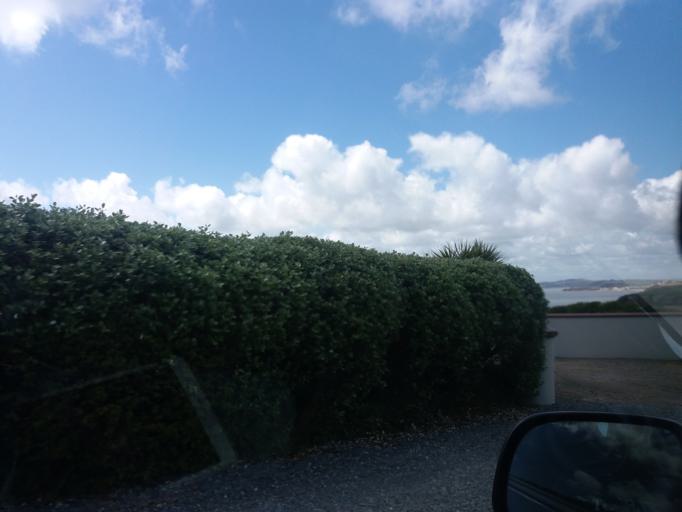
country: IE
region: Munster
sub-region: Waterford
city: Dunmore East
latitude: 52.1958
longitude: -6.8992
